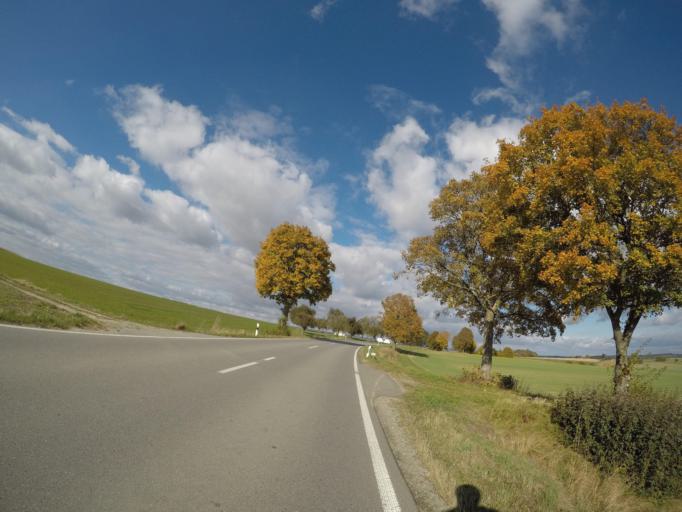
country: DE
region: Baden-Wuerttemberg
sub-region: Tuebingen Region
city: Oberstadion
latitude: 48.1738
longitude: 9.6880
